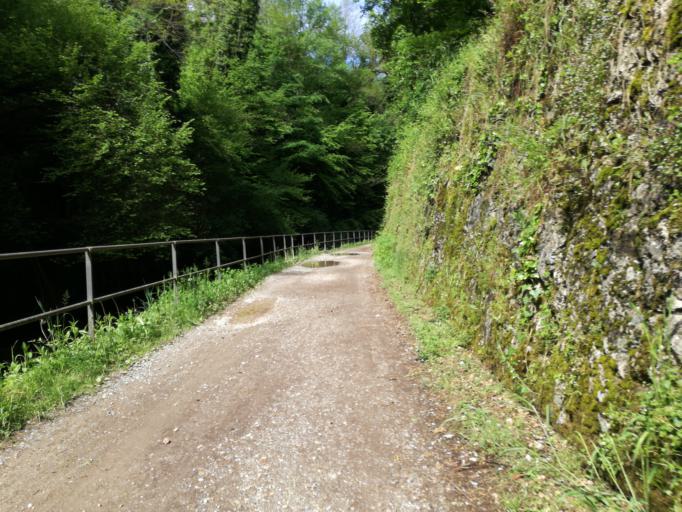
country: IT
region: Lombardy
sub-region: Provincia di Monza e Brianza
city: Porto d'Adda
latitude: 45.6689
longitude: 9.4696
